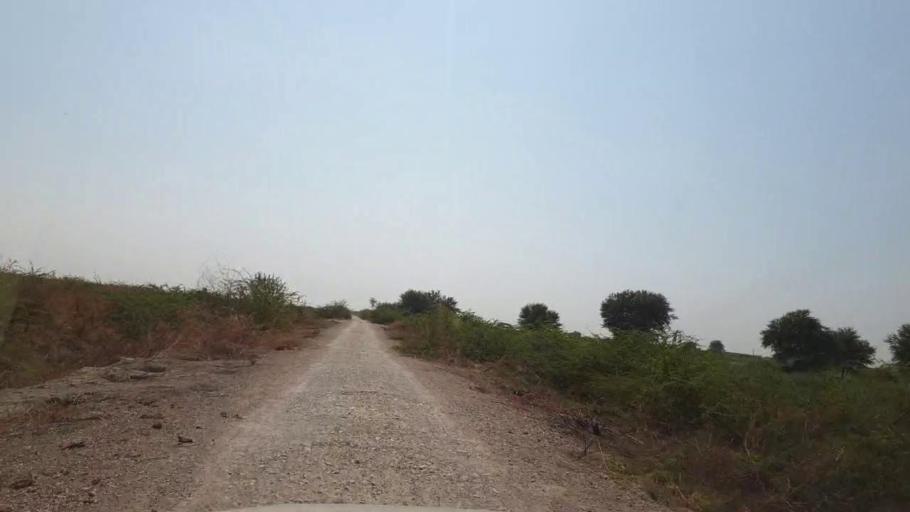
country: PK
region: Sindh
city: Kunri
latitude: 25.0946
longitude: 69.4742
